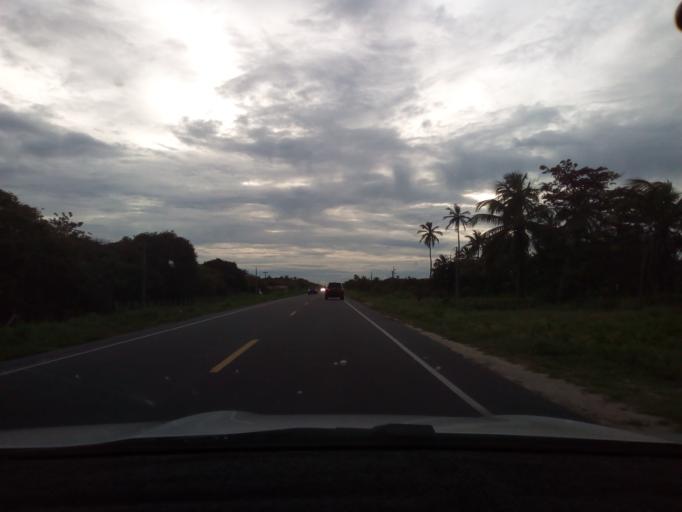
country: BR
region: Ceara
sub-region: Aracati
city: Aracati
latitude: -4.3701
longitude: -37.9389
